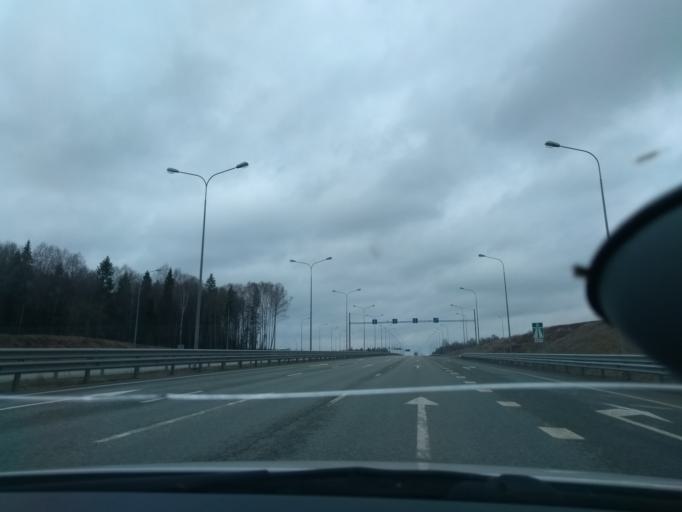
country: RU
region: Perm
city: Zvezdnyy
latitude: 57.7326
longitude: 56.3461
